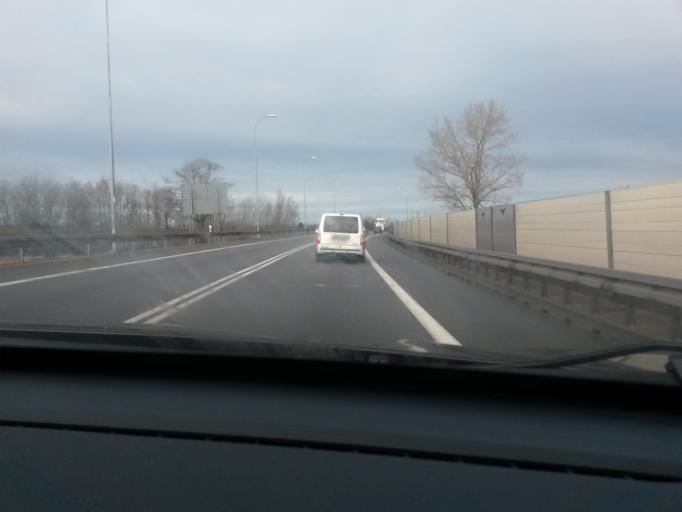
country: PL
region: Pomeranian Voivodeship
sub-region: Powiat nowodworski
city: Nowy Dwor Gdanski
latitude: 54.2010
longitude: 19.1134
